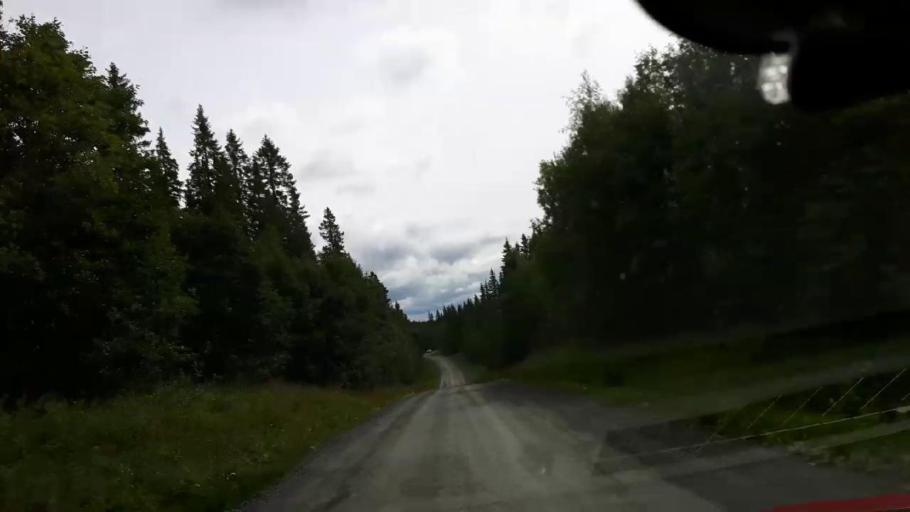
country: SE
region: Jaemtland
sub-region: Krokoms Kommun
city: Valla
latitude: 63.6678
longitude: 13.9617
